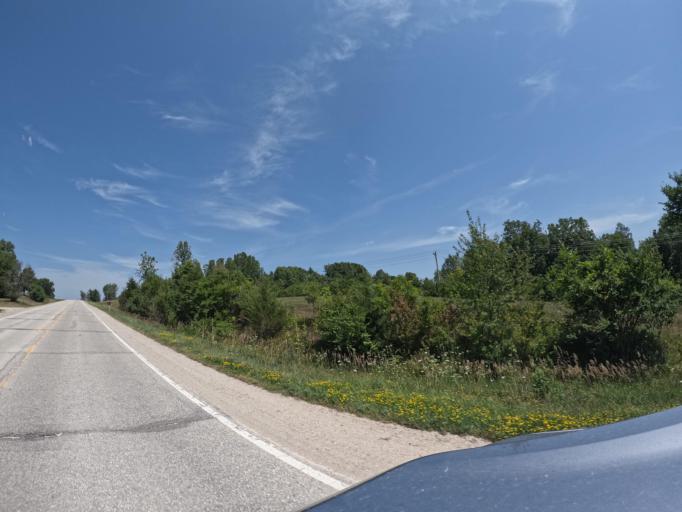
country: US
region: Iowa
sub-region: Henry County
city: Mount Pleasant
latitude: 40.9405
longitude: -91.6160
